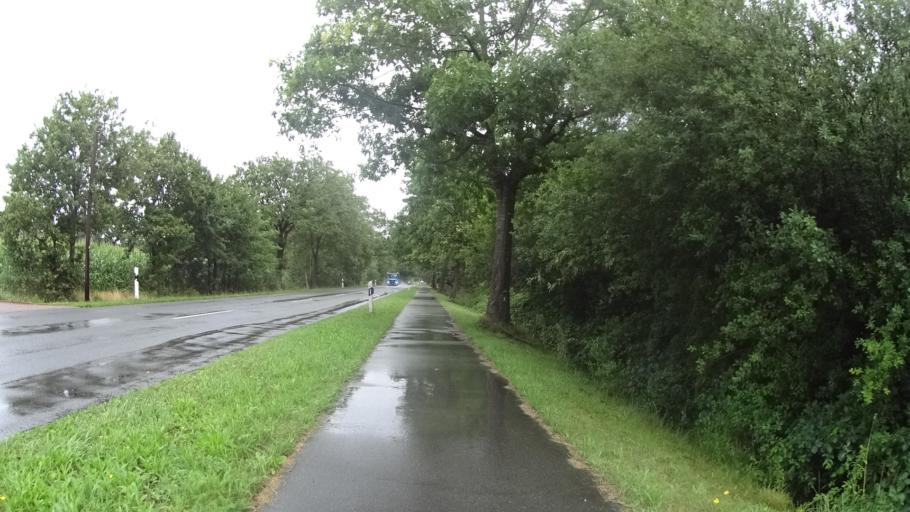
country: DE
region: Lower Saxony
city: Firrel
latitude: 53.3289
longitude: 7.6475
